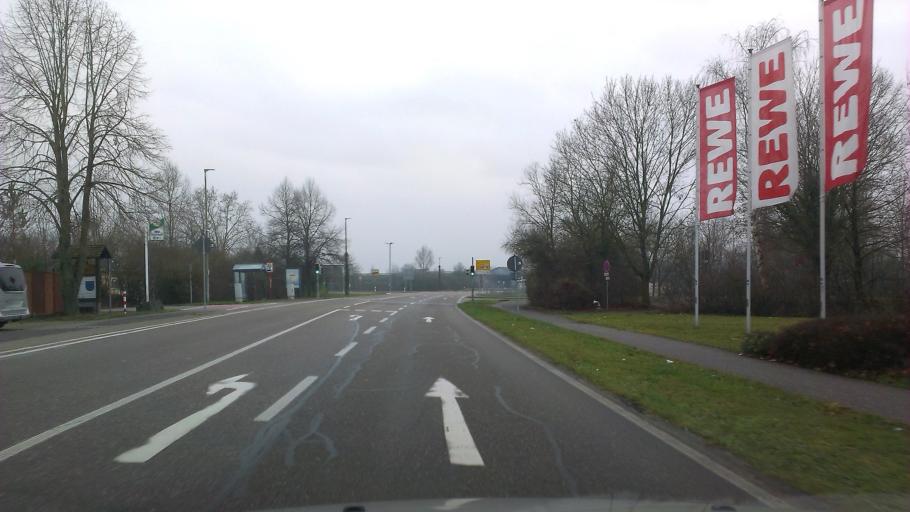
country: DE
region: Baden-Wuerttemberg
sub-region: Karlsruhe Region
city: Ubstadt-Weiher
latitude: 49.1716
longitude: 8.6184
